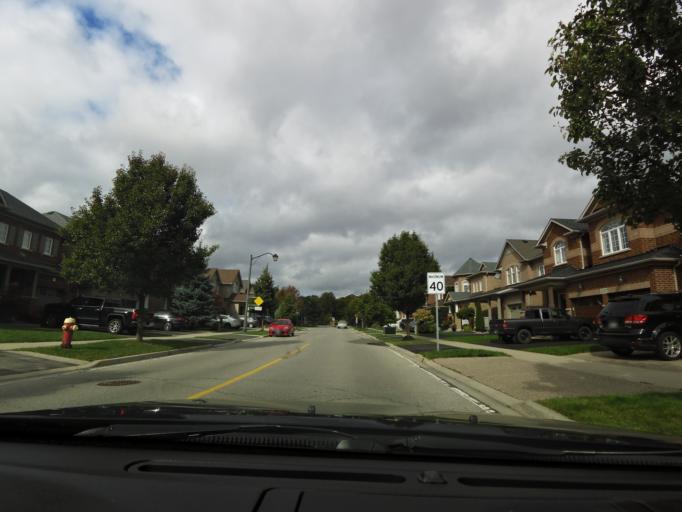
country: CA
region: Ontario
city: Burlington
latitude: 43.4020
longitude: -79.7863
